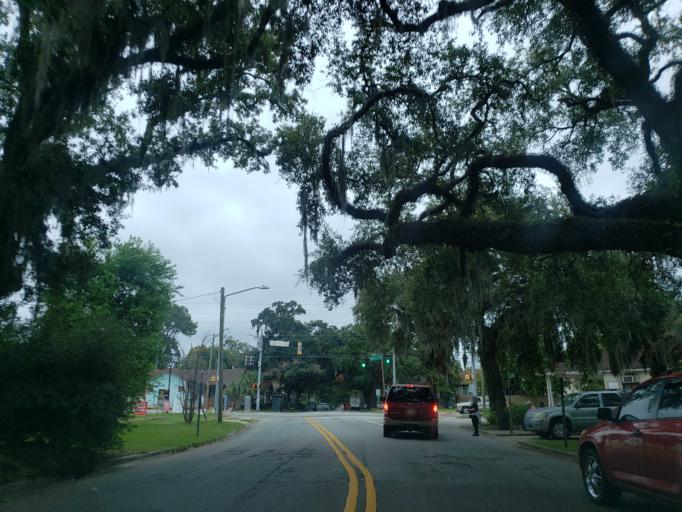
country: US
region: Georgia
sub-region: Chatham County
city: Savannah
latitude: 32.0529
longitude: -81.0843
